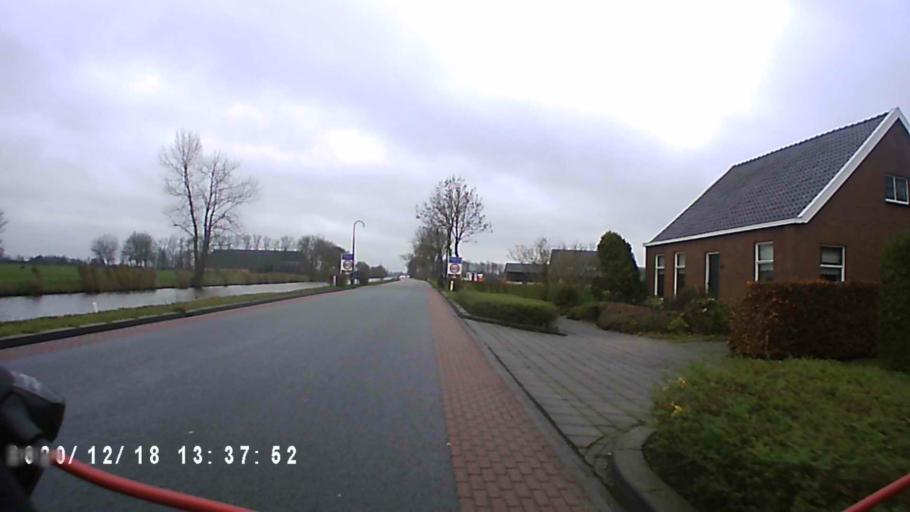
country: NL
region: Groningen
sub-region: Gemeente Bedum
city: Bedum
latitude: 53.3319
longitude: 6.5918
